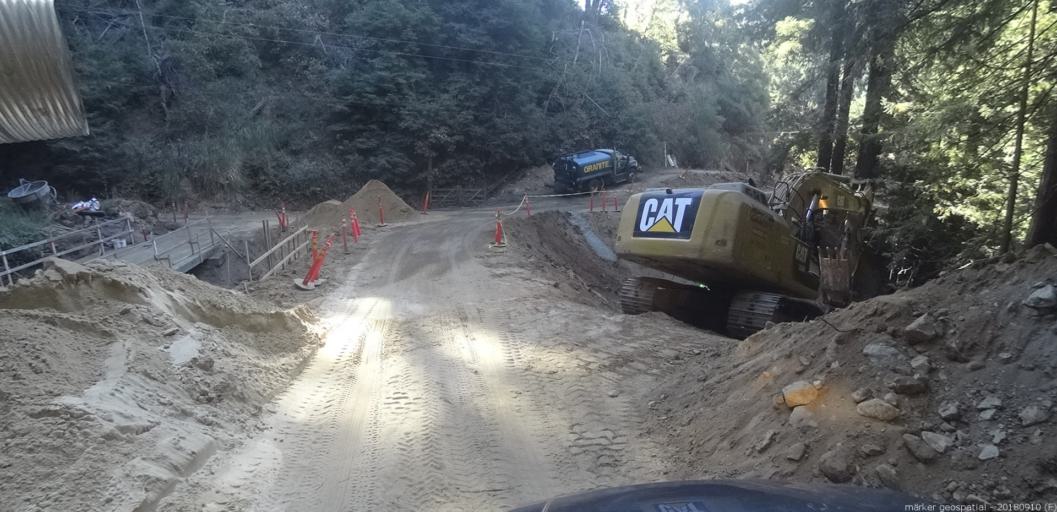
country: US
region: California
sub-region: Monterey County
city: Carmel Valley Village
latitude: 36.3834
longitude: -121.8647
